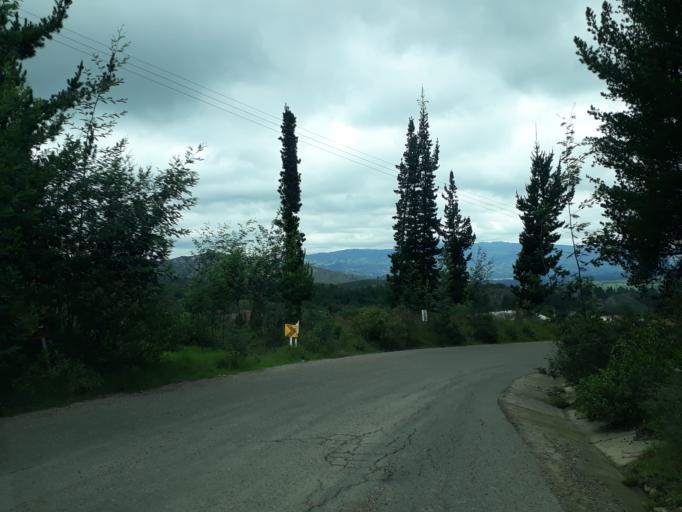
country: CO
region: Cundinamarca
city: Cucunuba
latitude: 5.2275
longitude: -73.7790
